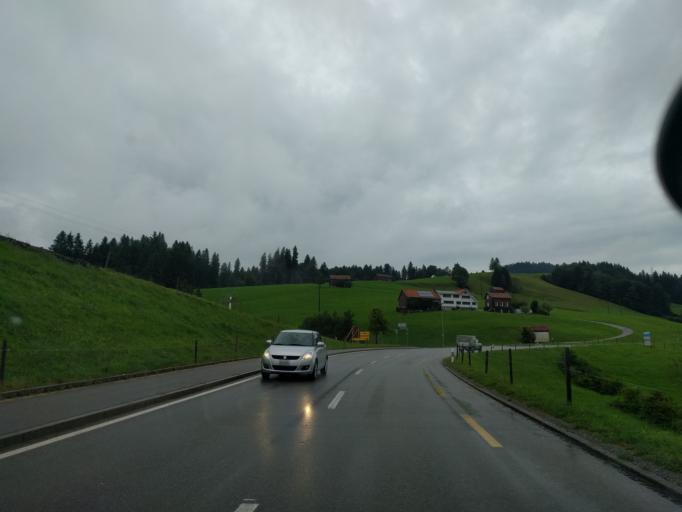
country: CH
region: Appenzell Ausserrhoden
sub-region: Bezirk Hinterland
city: Schwellbrunn
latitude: 47.3355
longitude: 9.2361
